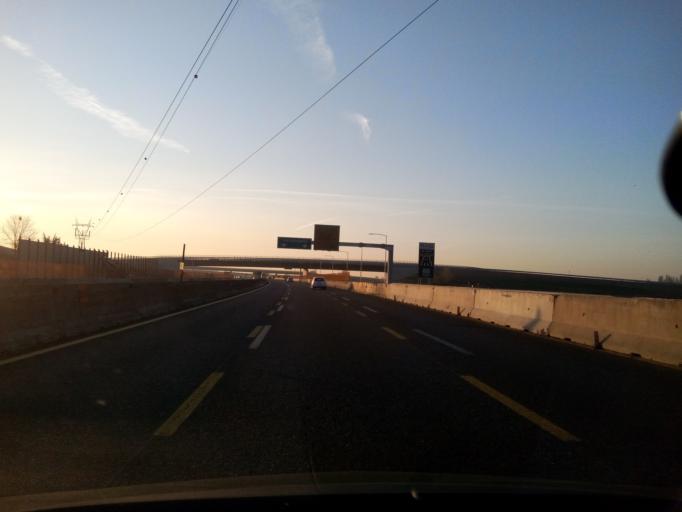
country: IT
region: Lombardy
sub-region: Citta metropolitana di Milano
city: Riozzo
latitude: 45.3424
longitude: 9.3186
